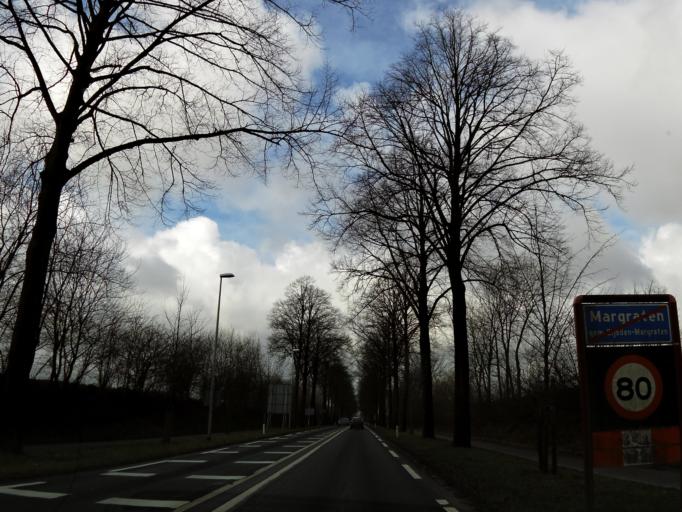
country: NL
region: Limburg
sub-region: Eijsden-Margraten
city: Margraten
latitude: 50.8192
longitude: 5.8175
